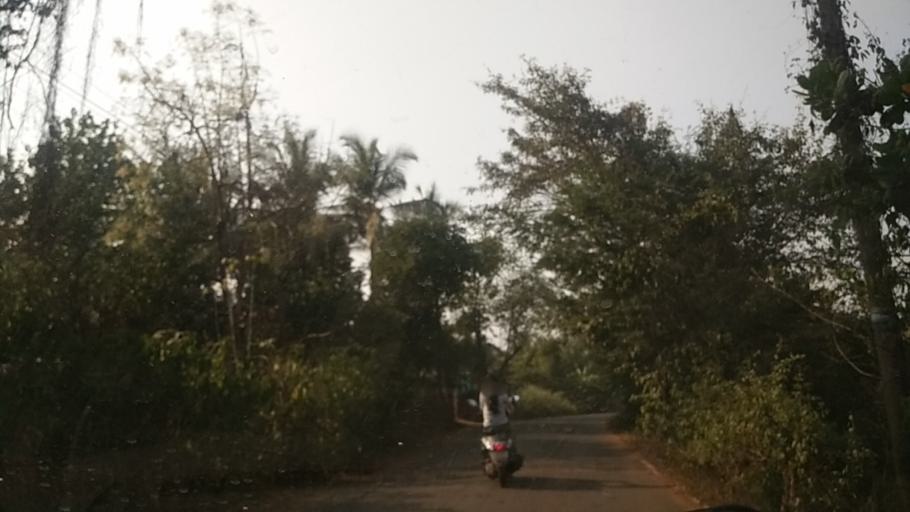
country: IN
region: Goa
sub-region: North Goa
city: Pernem
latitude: 15.7214
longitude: 73.7908
